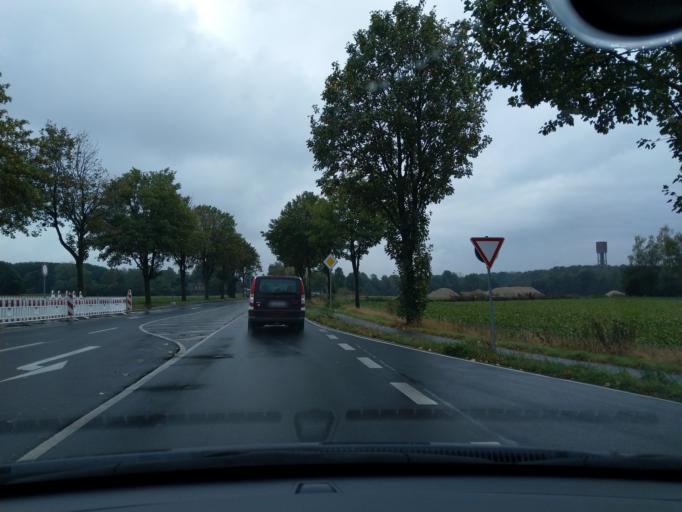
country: DE
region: North Rhine-Westphalia
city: Wegberg
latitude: 51.1315
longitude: 6.2838
